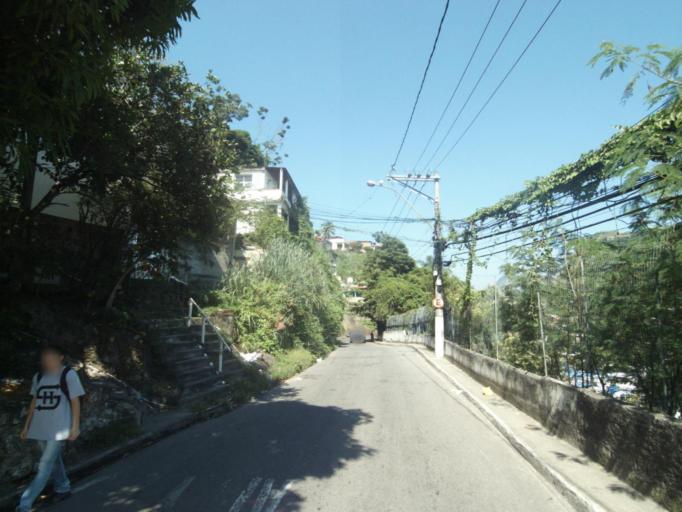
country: BR
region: Rio de Janeiro
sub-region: Niteroi
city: Niteroi
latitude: -22.9351
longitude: -43.1106
